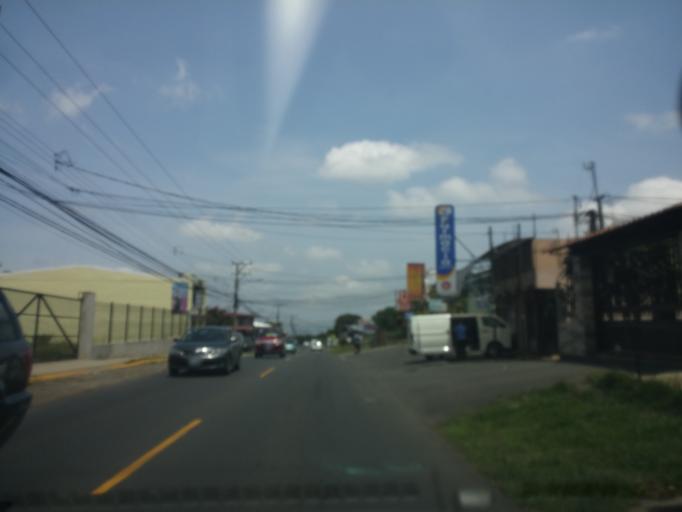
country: CR
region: Heredia
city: Llorente
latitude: 9.9988
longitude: -84.1558
